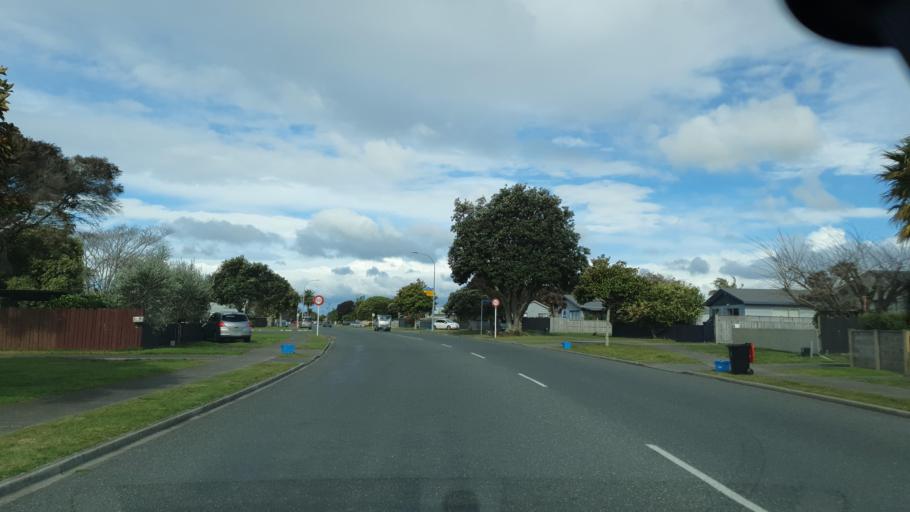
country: NZ
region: Bay of Plenty
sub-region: Tauranga City
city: Tauranga
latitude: -37.6968
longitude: 176.2645
